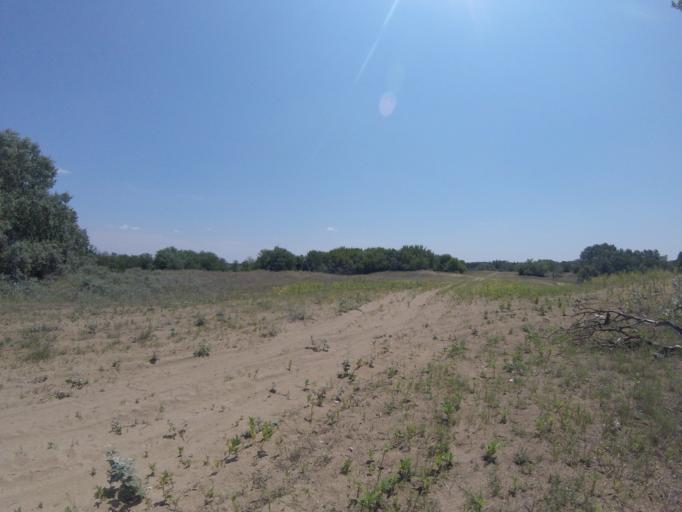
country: HU
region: Bacs-Kiskun
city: Jaszszentlaszlo
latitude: 46.6172
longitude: 19.7099
